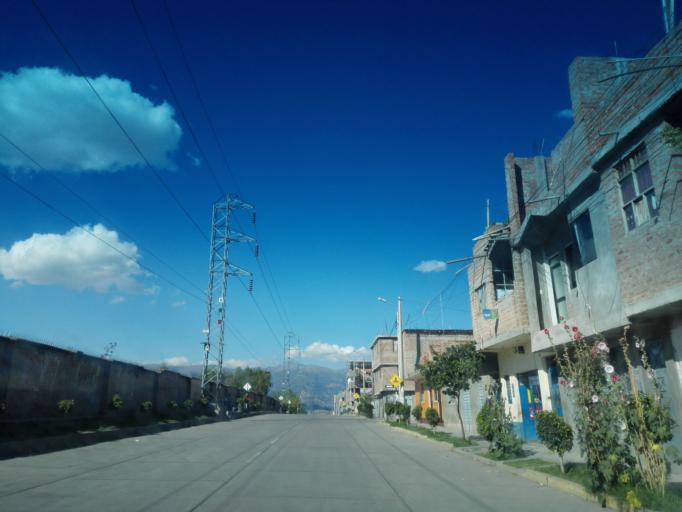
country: PE
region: Ayacucho
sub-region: Provincia de Huamanga
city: Ayacucho
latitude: -13.1503
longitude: -74.2173
